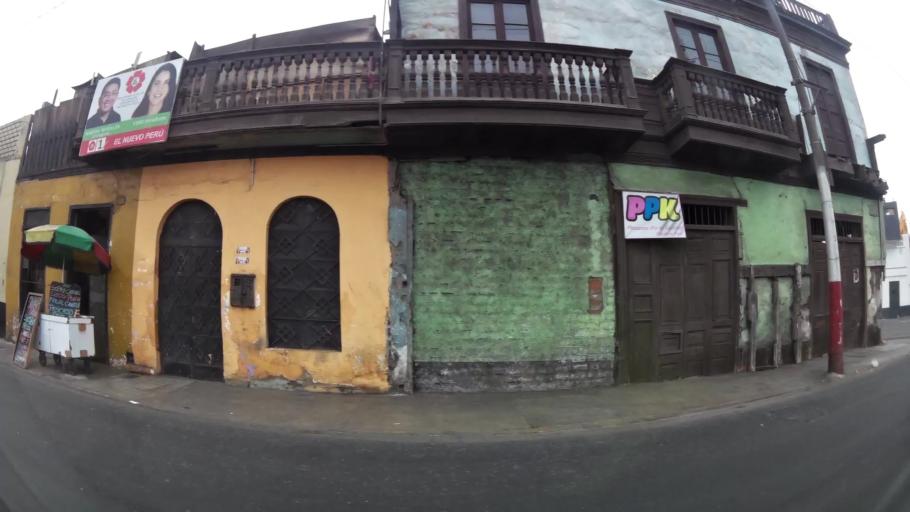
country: PE
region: Callao
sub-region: Callao
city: Callao
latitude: -12.0542
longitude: -77.1426
